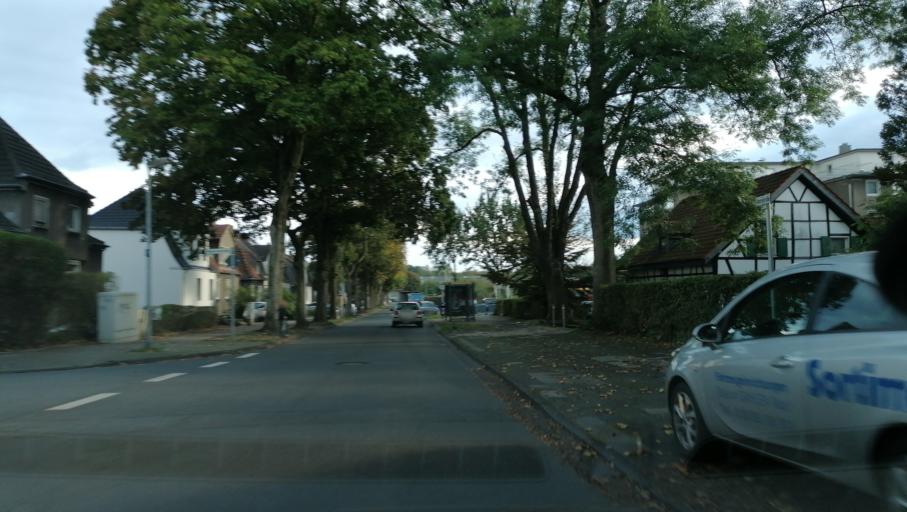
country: DE
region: North Rhine-Westphalia
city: Herten
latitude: 51.5728
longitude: 7.1117
